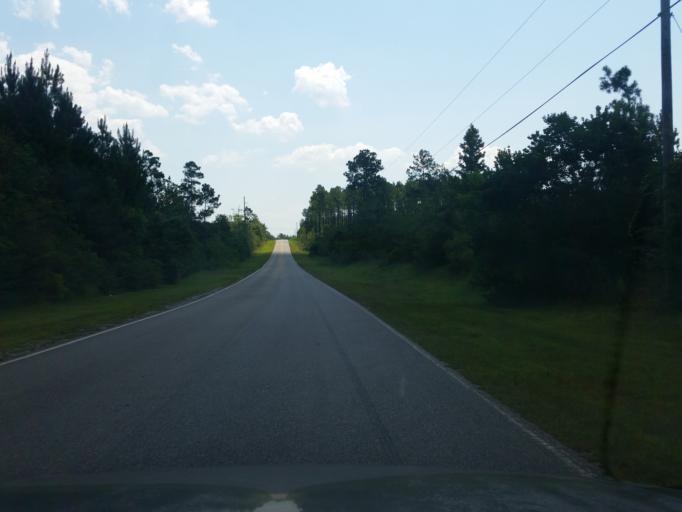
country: US
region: Florida
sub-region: Escambia County
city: Gonzalez
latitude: 30.6191
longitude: -87.2977
